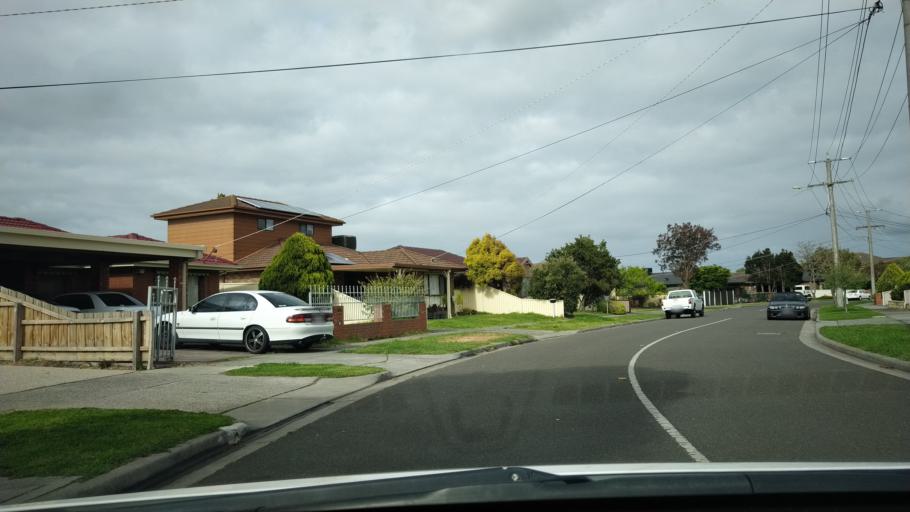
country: AU
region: Victoria
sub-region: Greater Dandenong
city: Keysborough
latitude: -37.9974
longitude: 145.1732
